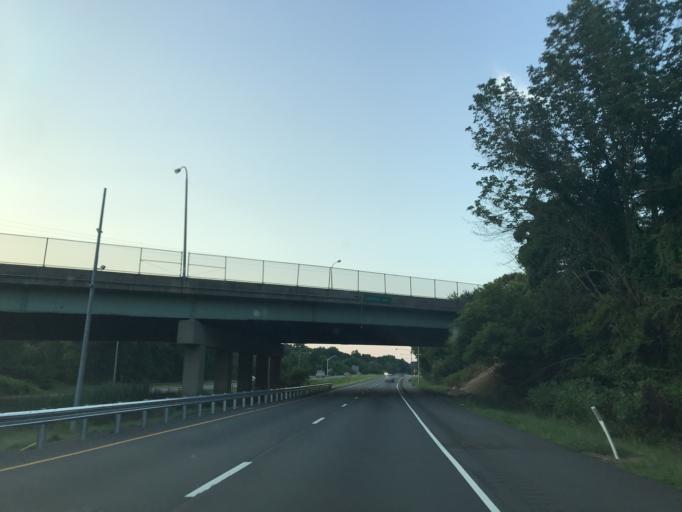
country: US
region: Pennsylvania
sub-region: Bucks County
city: Langhorne Manor
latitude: 40.1653
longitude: -74.9000
